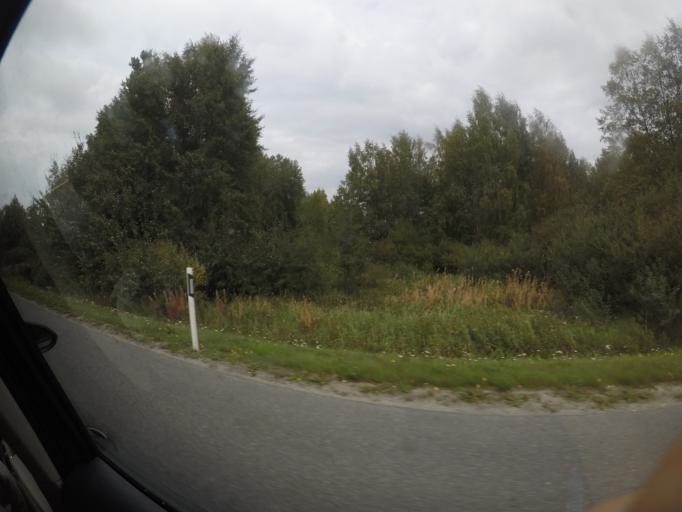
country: FI
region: Haeme
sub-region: Haemeenlinna
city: Parola
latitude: 61.0419
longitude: 24.4012
